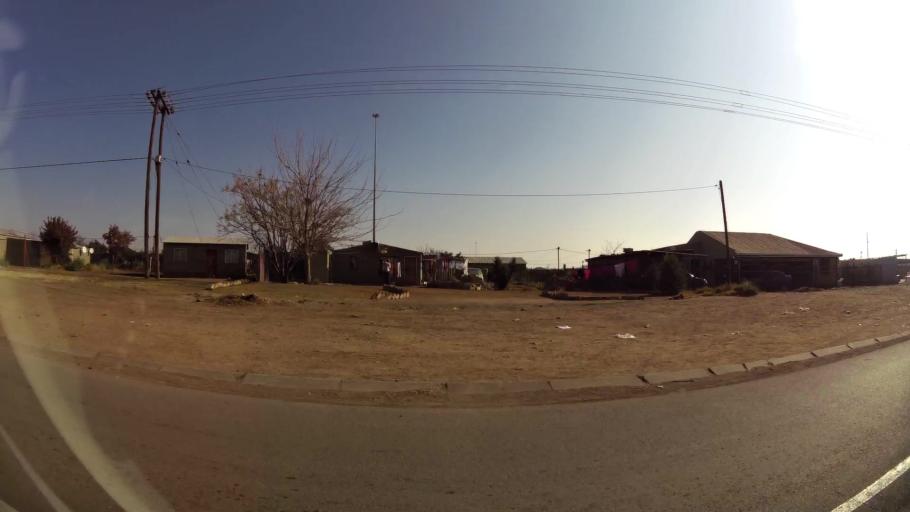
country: ZA
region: Orange Free State
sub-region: Mangaung Metropolitan Municipality
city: Bloemfontein
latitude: -29.1714
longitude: 26.2315
